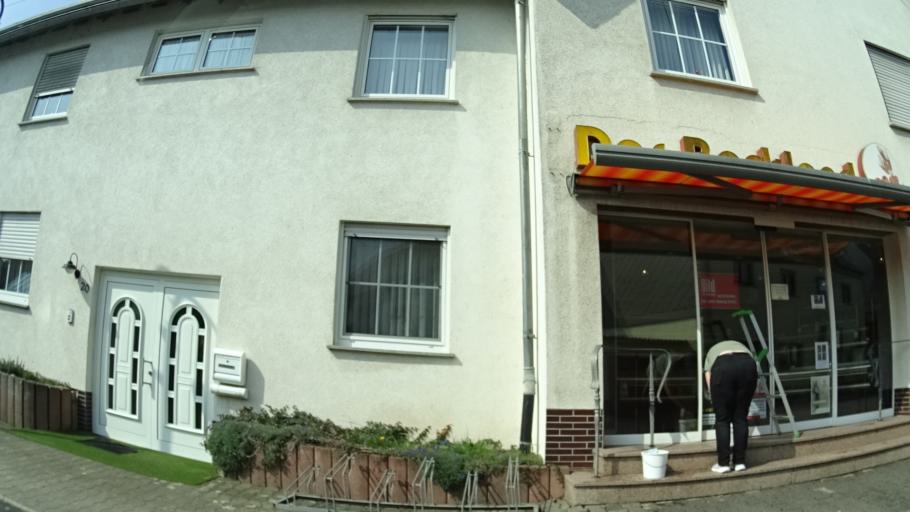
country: DE
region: Rheinland-Pfalz
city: Hoppstadten-Weiersbach
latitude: 49.6169
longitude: 7.1957
